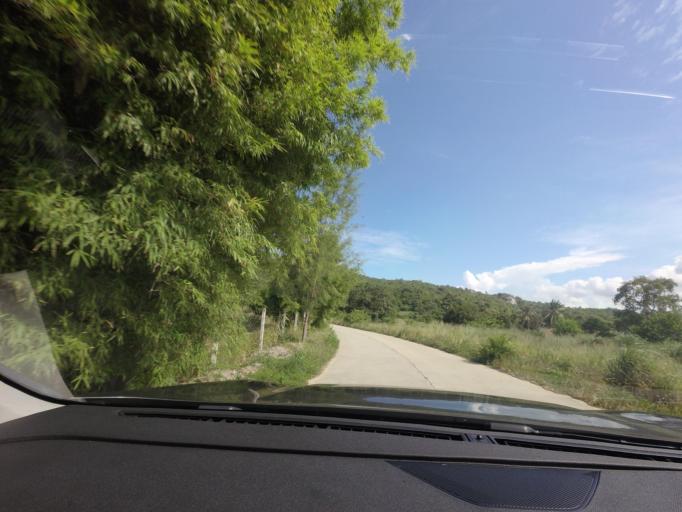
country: TH
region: Prachuap Khiri Khan
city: Hua Hin
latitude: 12.4852
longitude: 99.9415
